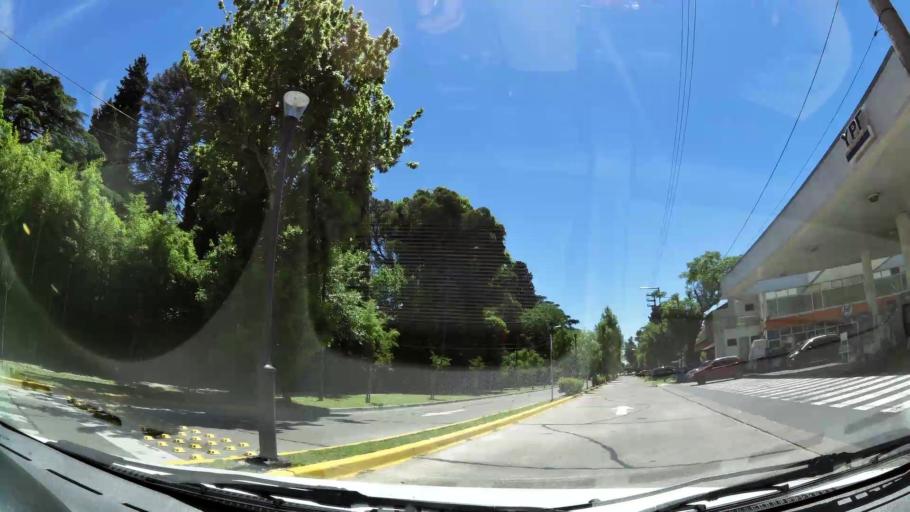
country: AR
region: Buenos Aires
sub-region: Partido de San Isidro
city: San Isidro
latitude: -34.5024
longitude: -58.5608
